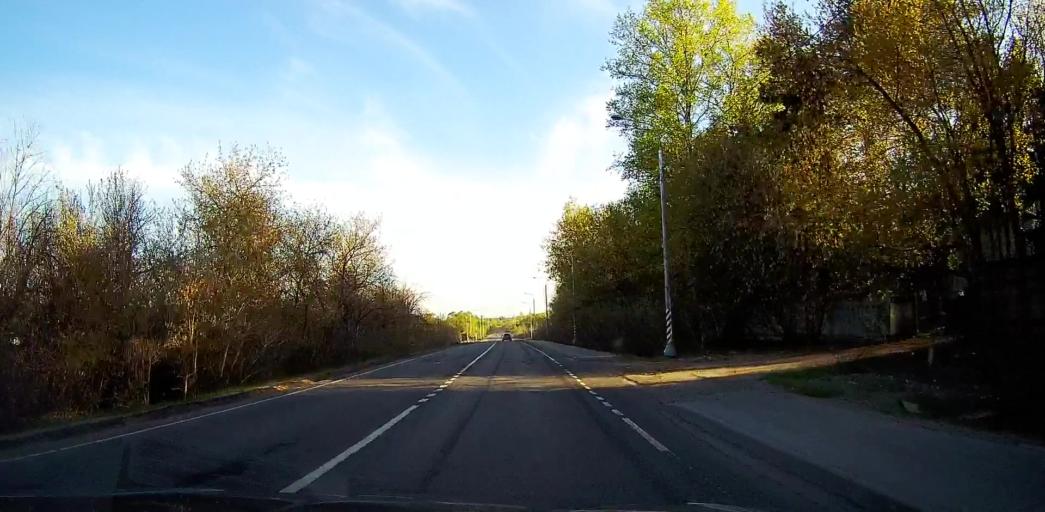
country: RU
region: Moskovskaya
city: Bronnitsy
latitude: 55.3098
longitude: 38.2139
